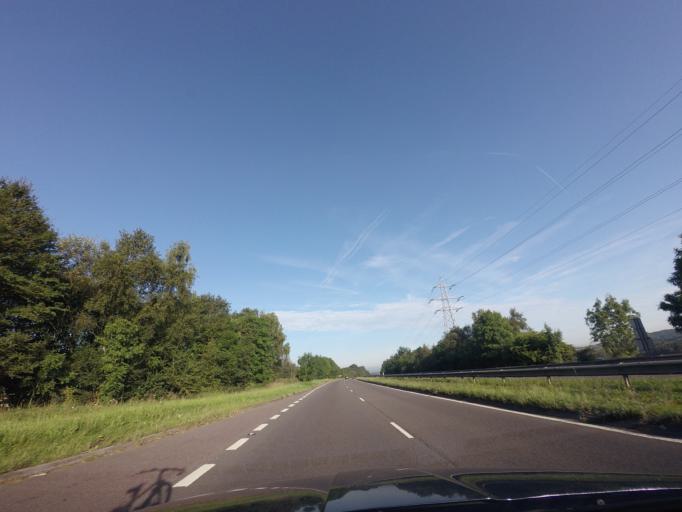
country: GB
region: England
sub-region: Derbyshire
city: Pilsley
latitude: 53.2029
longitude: -1.3670
